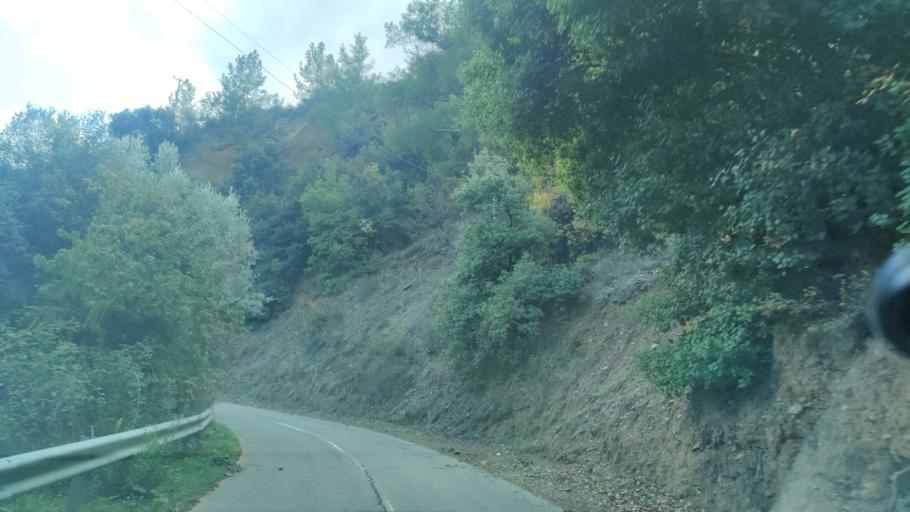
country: CY
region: Lefkosia
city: Lefka
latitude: 35.0580
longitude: 32.7337
